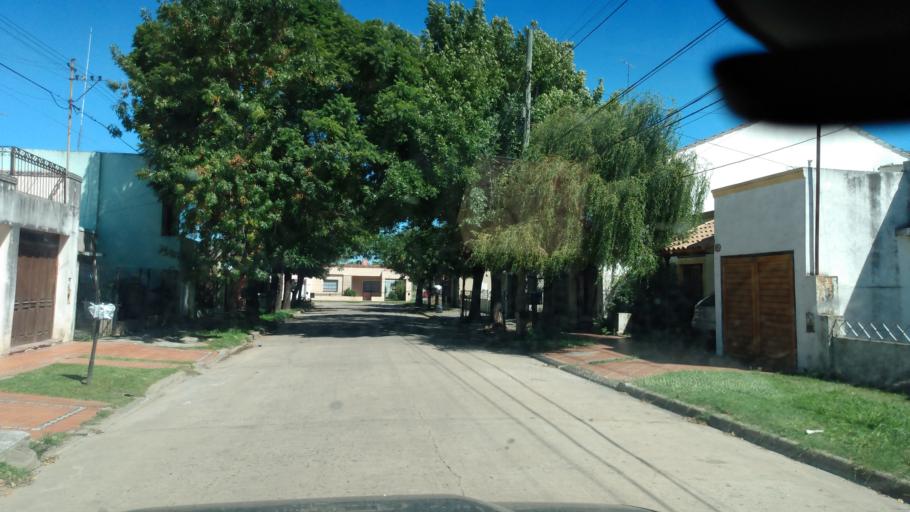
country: AR
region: Buenos Aires
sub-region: Partido de Lujan
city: Lujan
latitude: -34.5789
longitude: -59.1116
